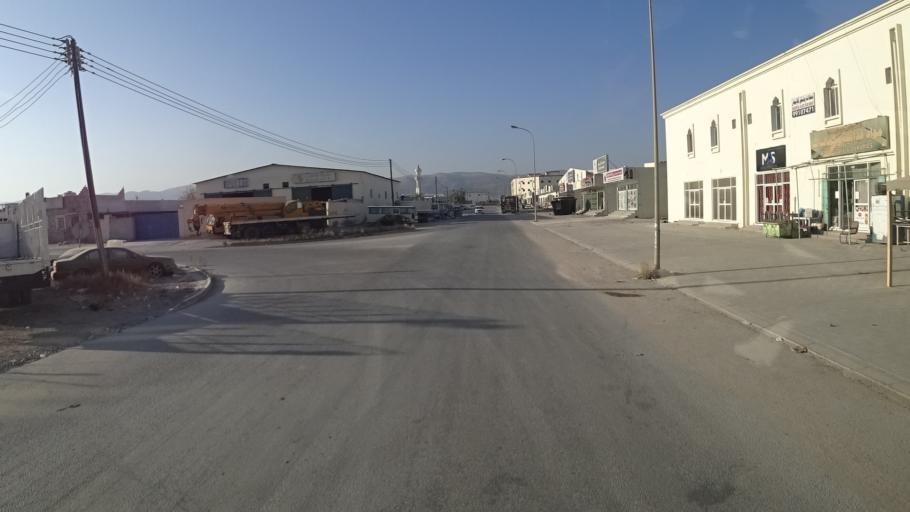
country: OM
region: Zufar
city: Salalah
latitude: 17.0220
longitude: 54.0459
